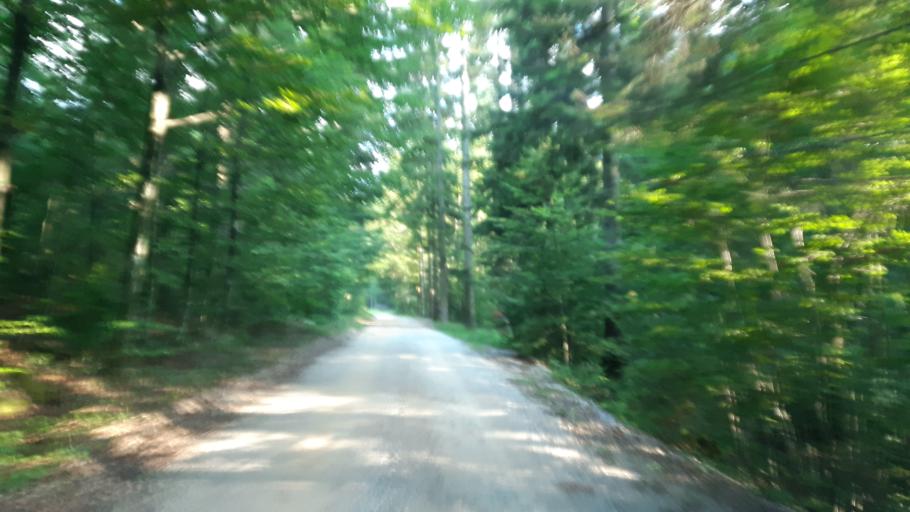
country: SI
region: Dolenjske Toplice
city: Dolenjske Toplice
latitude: 45.6896
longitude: 15.0051
